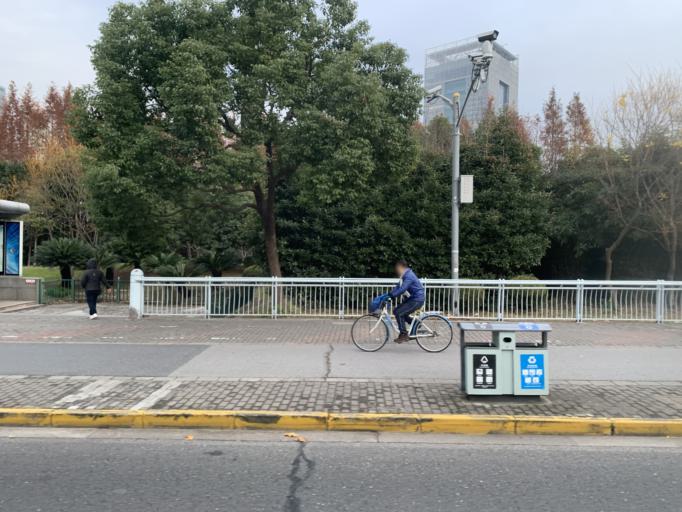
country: CN
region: Shanghai Shi
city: Pudong
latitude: 31.2216
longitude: 121.5248
